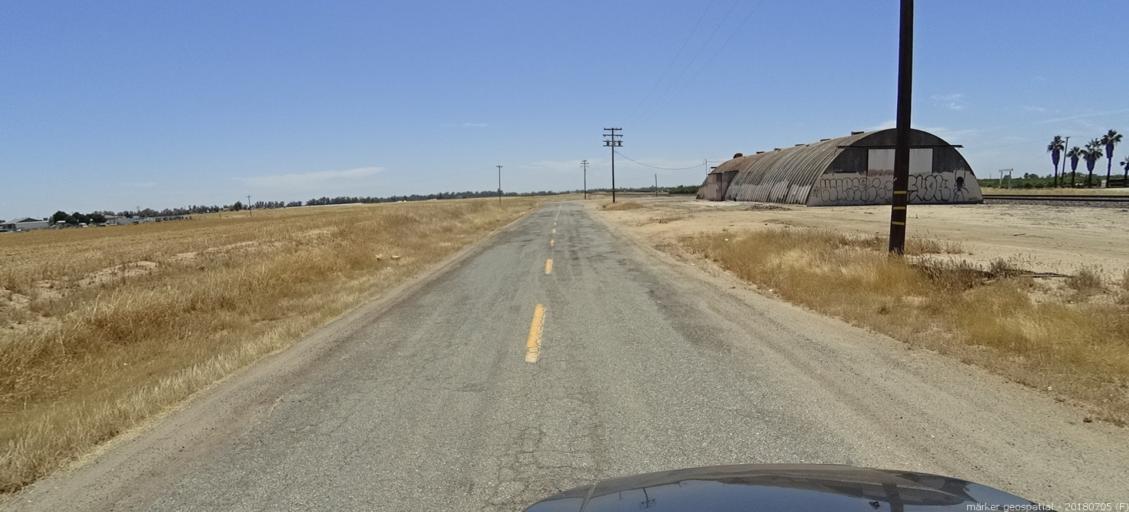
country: US
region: California
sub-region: Madera County
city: Madera Acres
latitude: 37.0485
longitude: -120.0941
